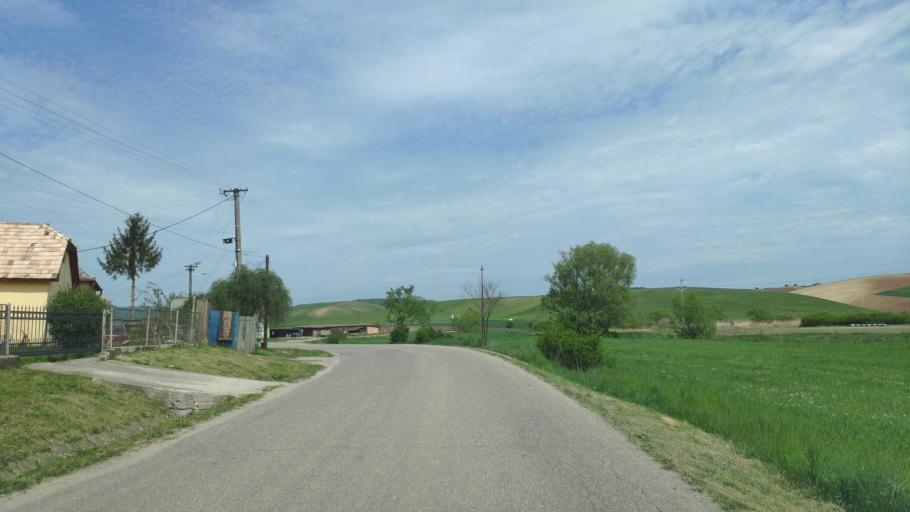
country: SK
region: Banskobystricky
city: Rimavska Sobota
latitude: 48.4222
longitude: 20.2281
